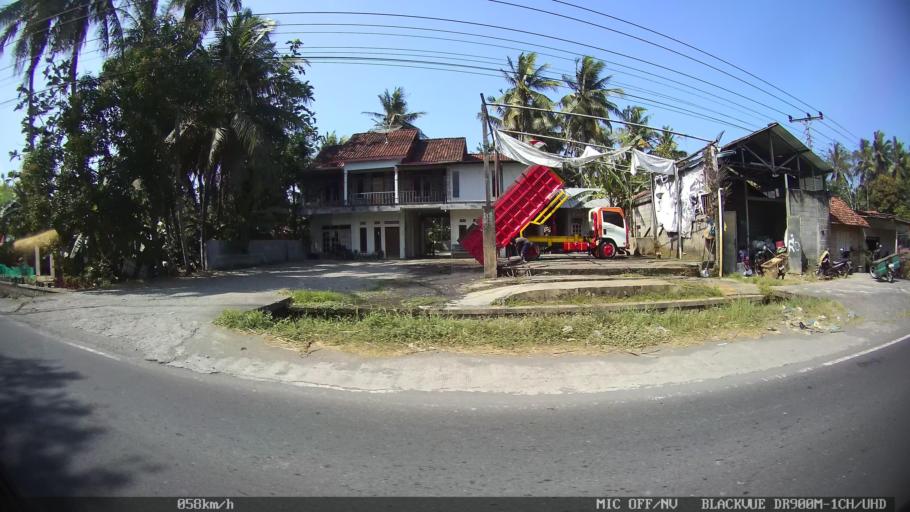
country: ID
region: Daerah Istimewa Yogyakarta
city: Srandakan
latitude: -7.9298
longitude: 110.1975
